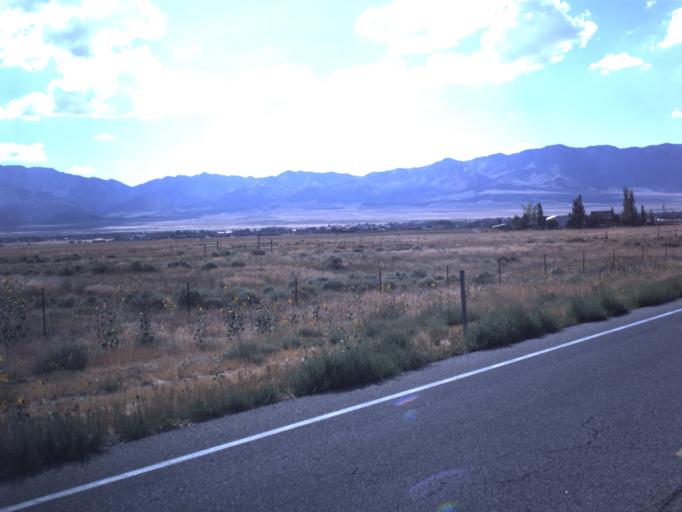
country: US
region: Utah
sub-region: Tooele County
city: Grantsville
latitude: 40.5844
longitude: -112.4070
